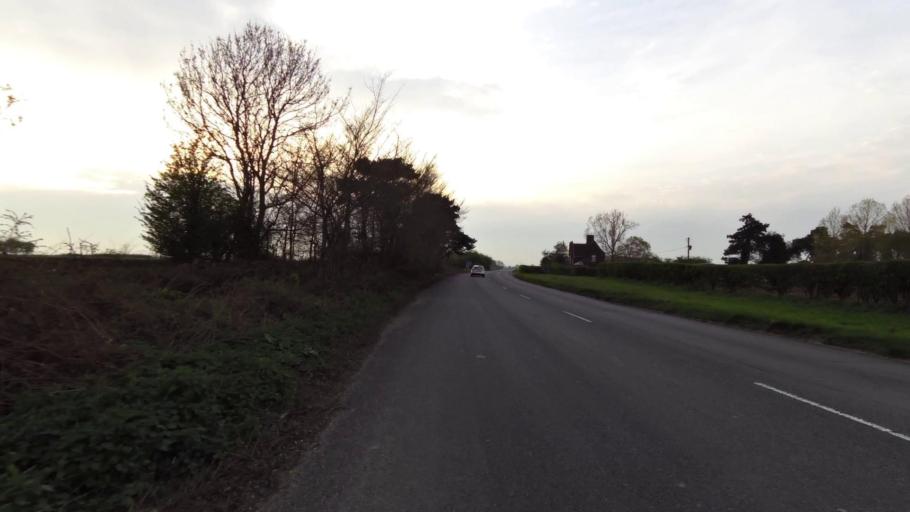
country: GB
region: England
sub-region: Suffolk
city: Shotley Gate
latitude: 52.0101
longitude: 1.2740
